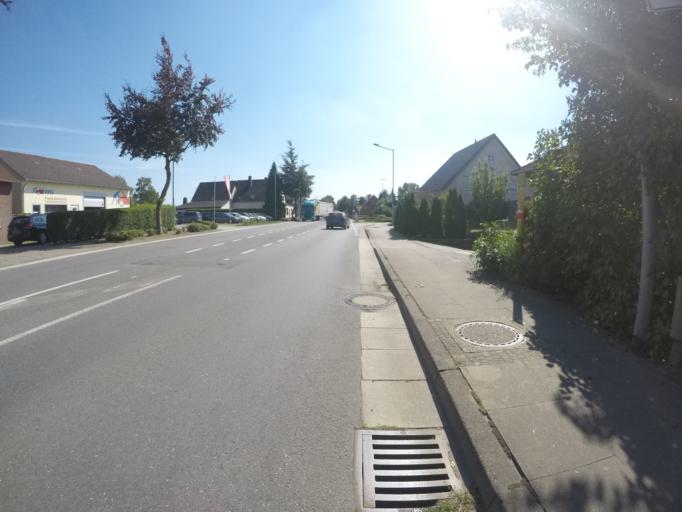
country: DE
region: North Rhine-Westphalia
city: Bad Oeynhausen
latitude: 52.1873
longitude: 8.7625
